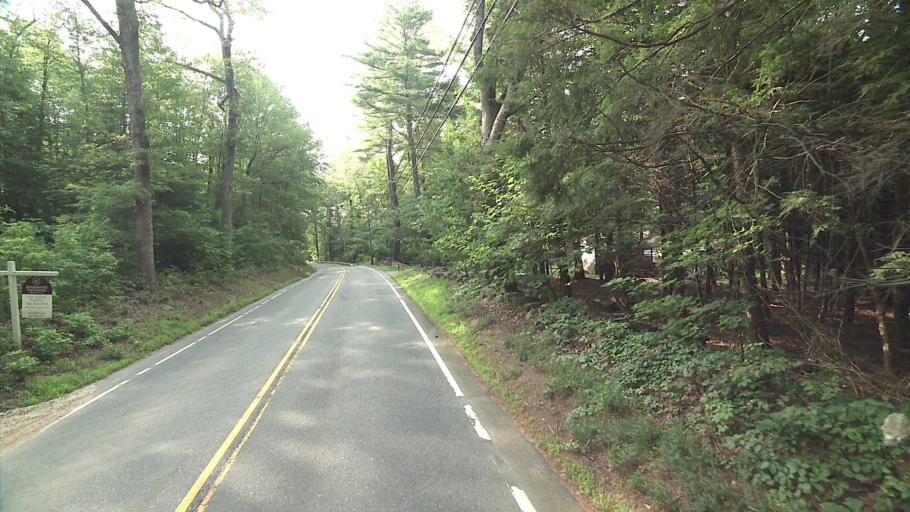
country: US
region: Massachusetts
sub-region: Worcester County
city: Southbridge
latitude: 41.9755
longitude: -72.0713
